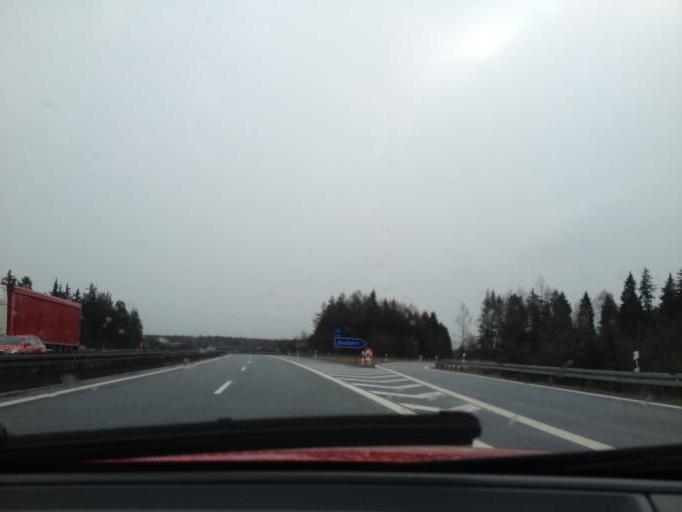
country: DE
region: Bavaria
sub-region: Upper Franconia
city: Schonwald
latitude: 50.2153
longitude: 12.0912
